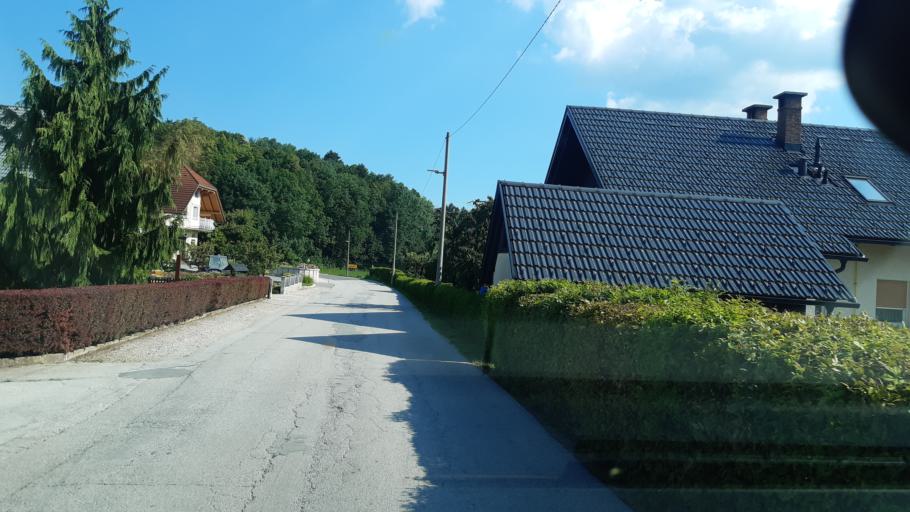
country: SI
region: Radovljica
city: Radovljica
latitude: 46.3627
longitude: 14.1938
